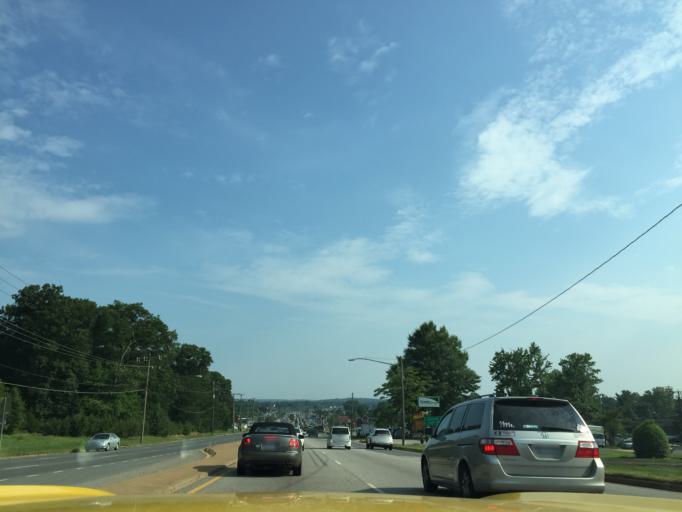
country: US
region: Virginia
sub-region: Fairfax County
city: Groveton
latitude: 38.7618
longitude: -77.0841
